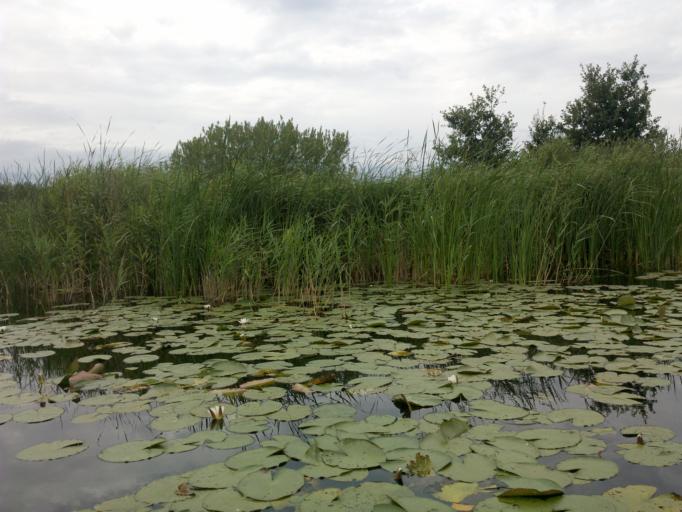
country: NL
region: North Holland
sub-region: Gemeente Wijdemeren
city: Kortenhoef
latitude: 52.2379
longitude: 5.0846
